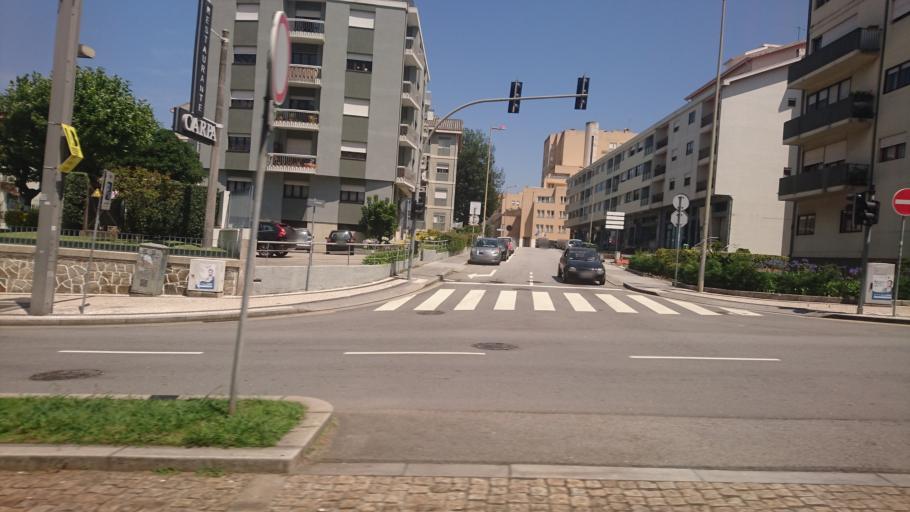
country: PT
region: Porto
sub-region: Vila Nova de Gaia
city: Vila Nova de Gaia
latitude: 41.1227
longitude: -8.6059
